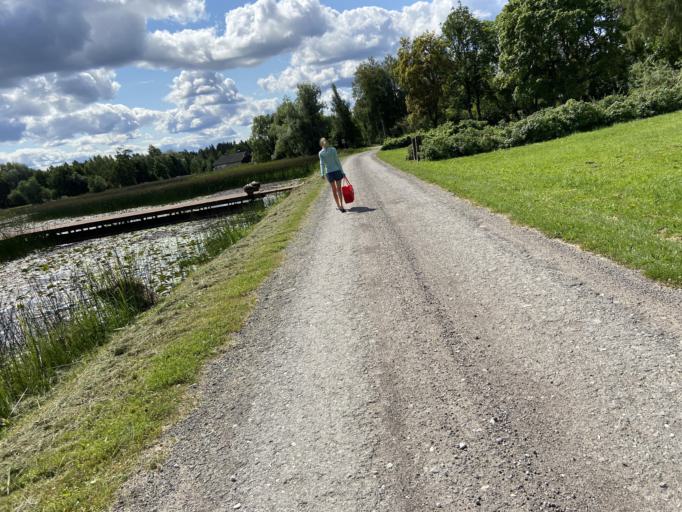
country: EE
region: Harju
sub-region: Keila linn
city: Keila
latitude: 59.1569
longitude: 24.4930
